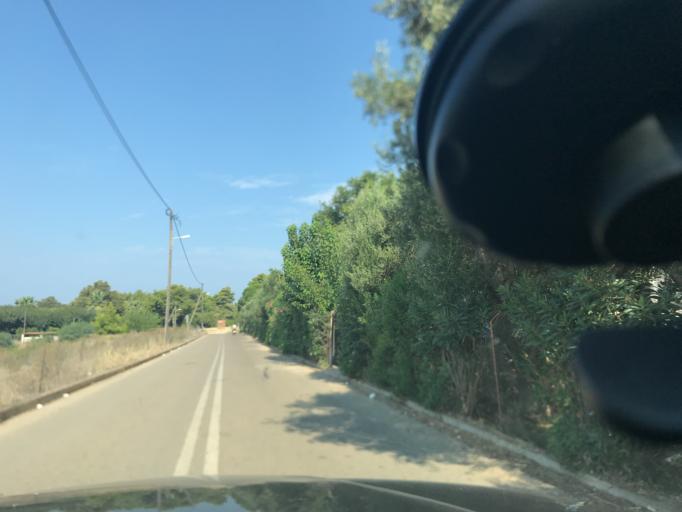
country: GR
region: West Greece
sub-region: Nomos Ileias
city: Kardamas
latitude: 37.7194
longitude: 21.3178
